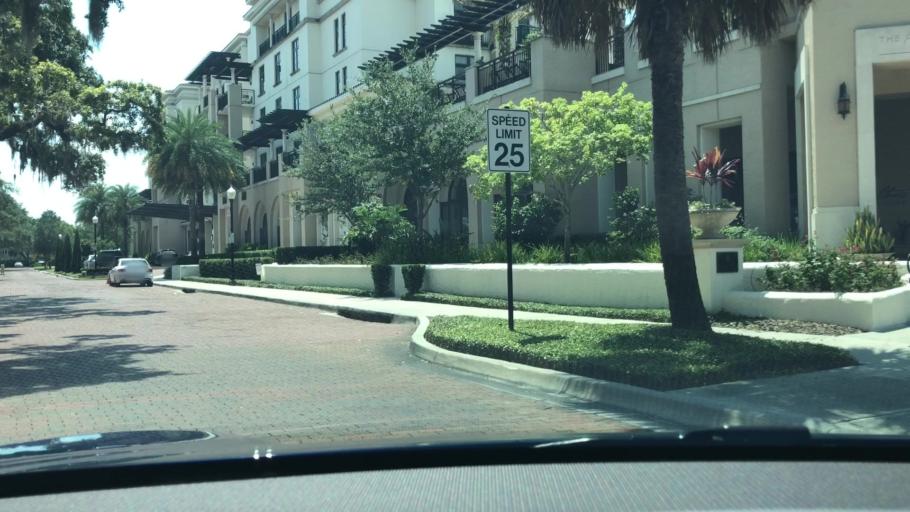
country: US
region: Florida
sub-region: Orange County
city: Winter Park
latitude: 28.5959
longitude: -81.3485
